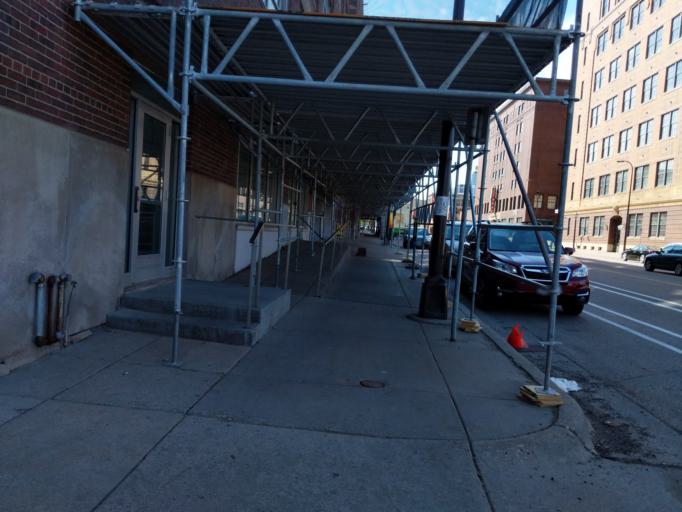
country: US
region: Minnesota
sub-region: Hennepin County
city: Minneapolis
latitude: 44.9881
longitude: -93.2777
